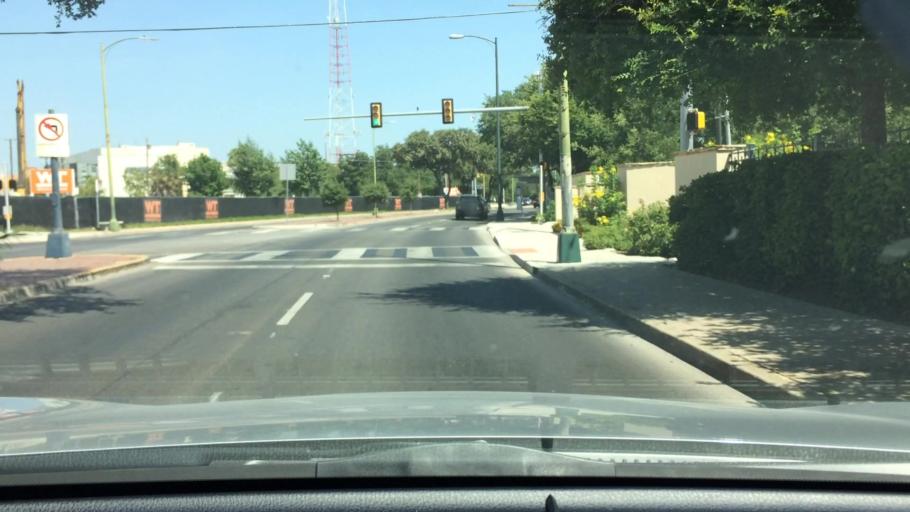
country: US
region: Texas
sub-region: Bexar County
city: San Antonio
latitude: 29.4196
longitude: -98.4957
